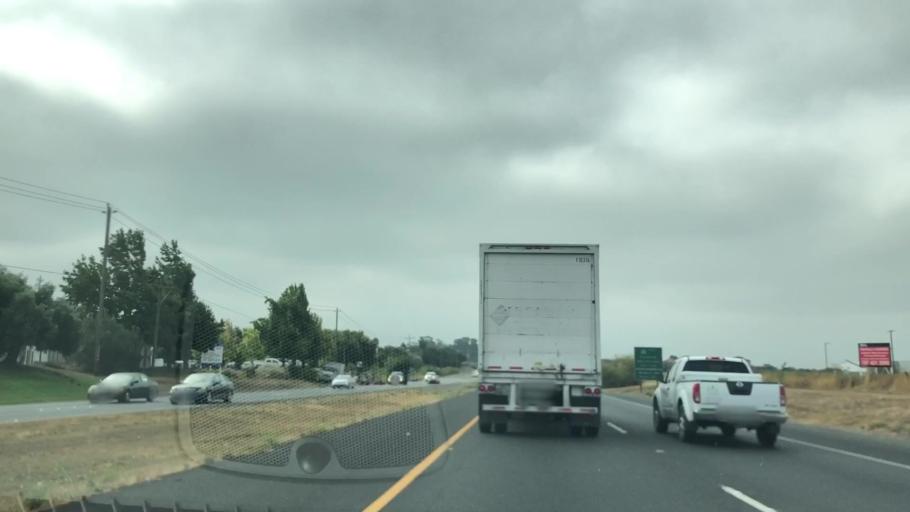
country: US
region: California
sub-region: Napa County
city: American Canyon
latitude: 38.2294
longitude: -122.2585
